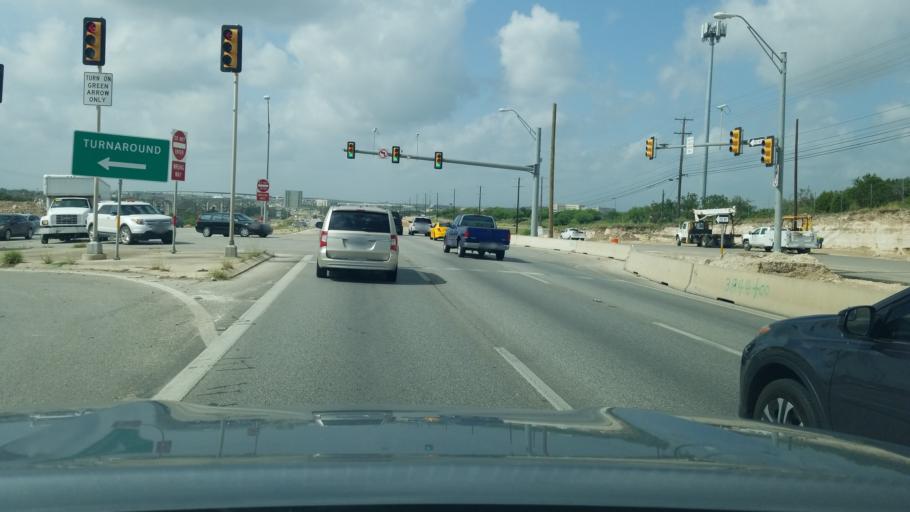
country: US
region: Texas
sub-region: Bexar County
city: Hollywood Park
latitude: 29.6303
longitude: -98.4608
